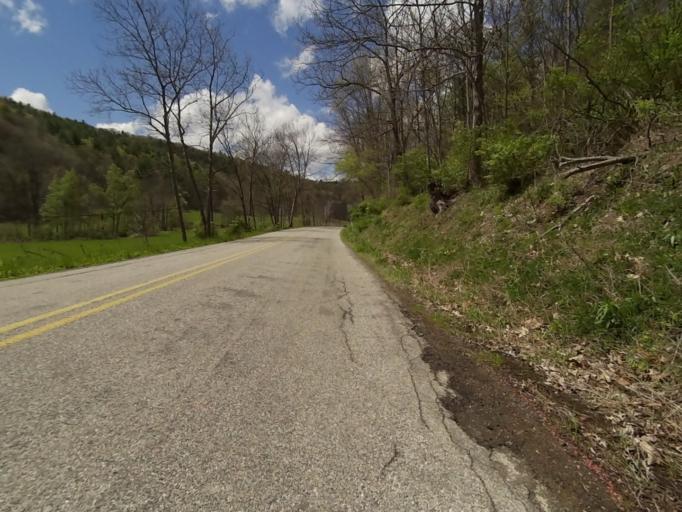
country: US
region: Pennsylvania
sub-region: Centre County
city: Milesburg
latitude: 40.9266
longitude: -77.8709
